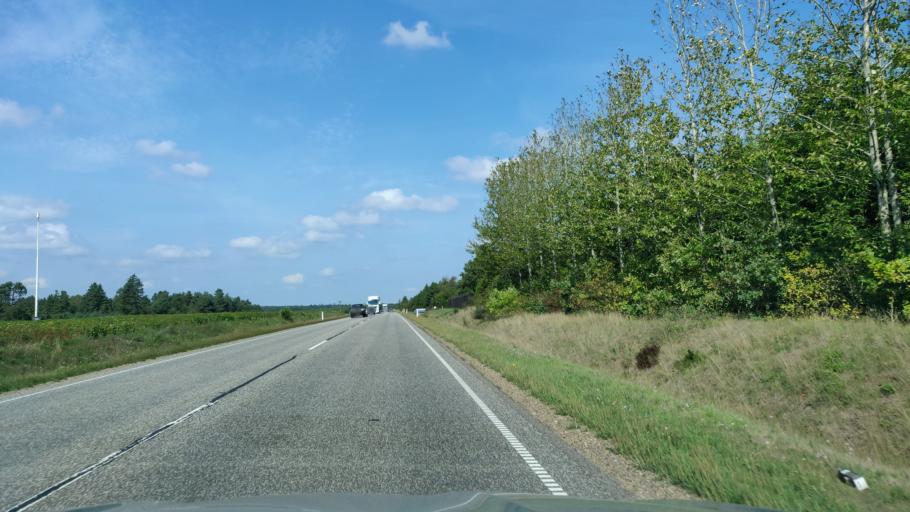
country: DK
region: Central Jutland
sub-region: Herning Kommune
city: Sunds
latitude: 56.3385
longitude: 8.9811
